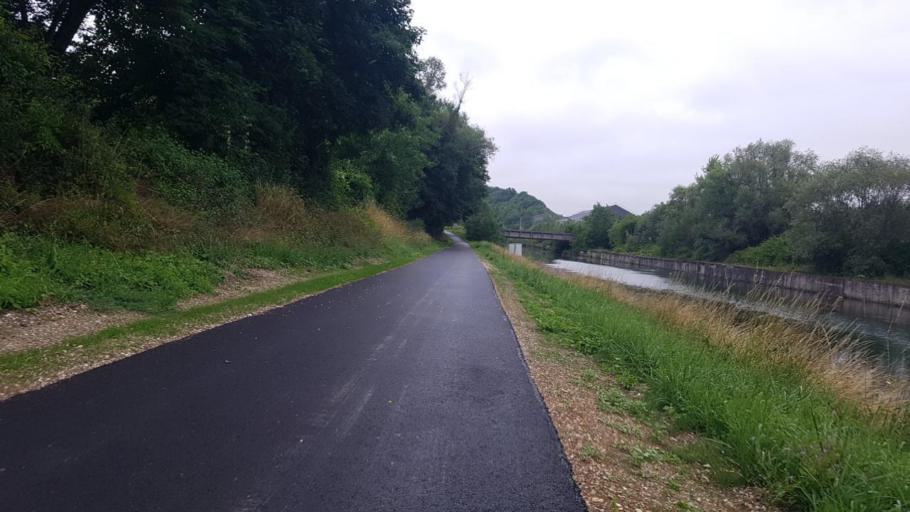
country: FR
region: Champagne-Ardenne
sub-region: Departement de la Marne
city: Vitry-le-Francois
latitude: 48.7637
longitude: 4.5612
